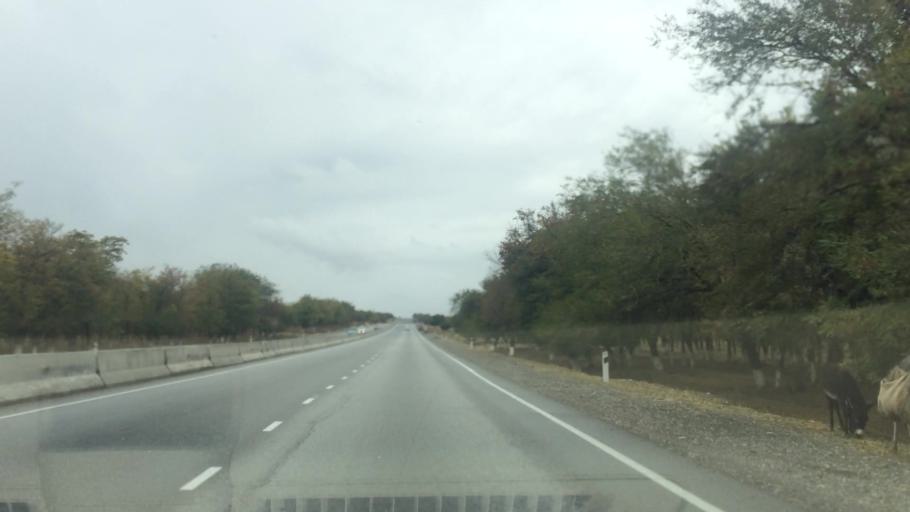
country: UZ
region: Samarqand
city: Bulung'ur
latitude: 39.8689
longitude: 67.4766
